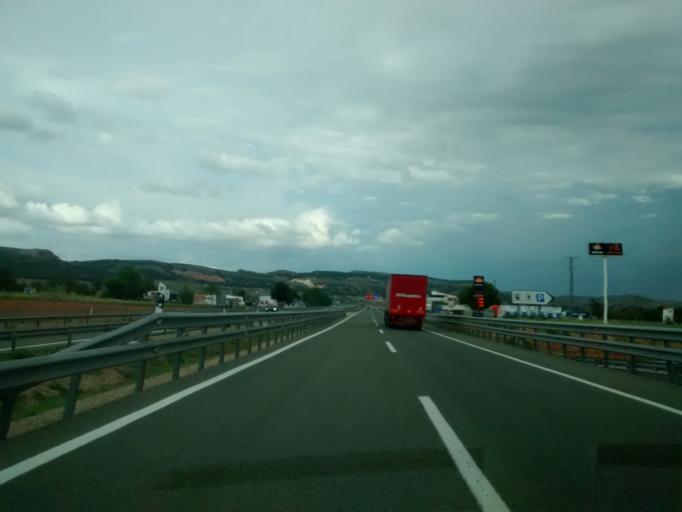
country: ES
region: Aragon
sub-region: Provincia de Zaragoza
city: Cetina
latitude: 41.3028
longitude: -1.9494
